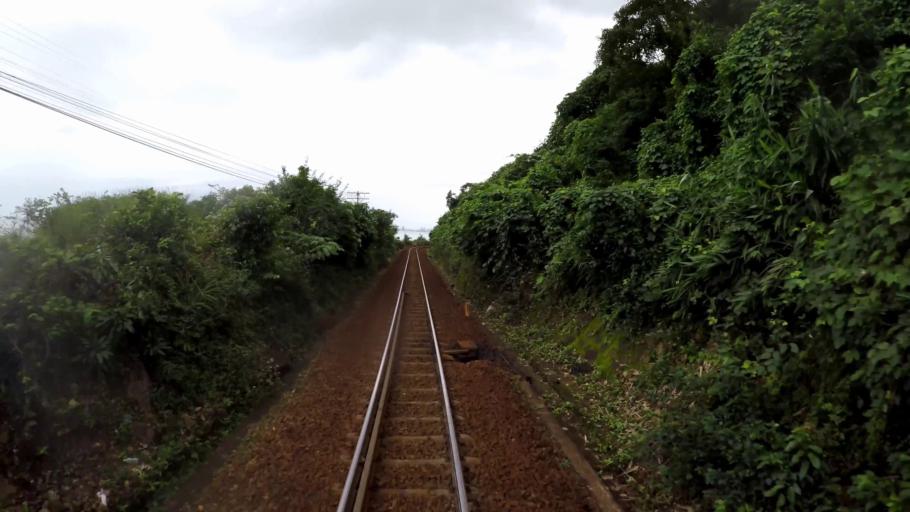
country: VN
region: Da Nang
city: Lien Chieu
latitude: 16.1560
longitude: 108.1354
